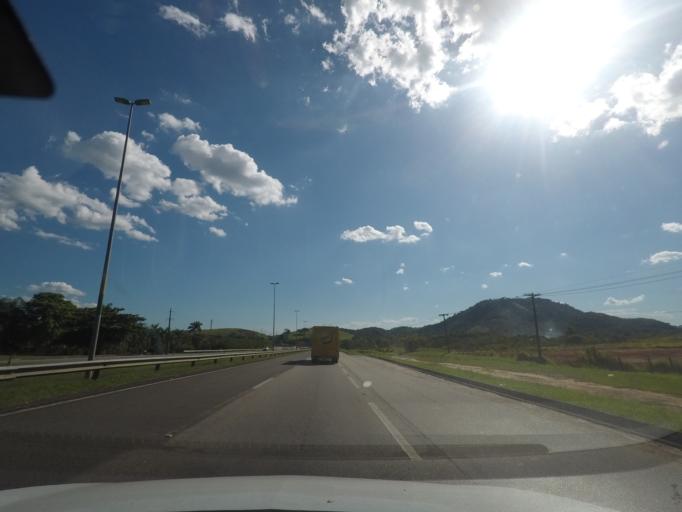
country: BR
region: Rio de Janeiro
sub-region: Guapimirim
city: Guapimirim
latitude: -22.5847
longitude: -43.0161
